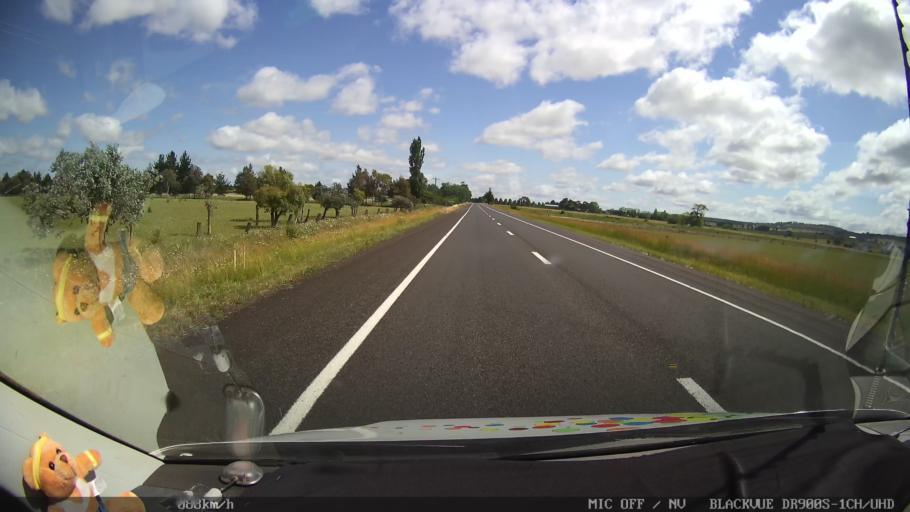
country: AU
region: New South Wales
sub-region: Glen Innes Severn
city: Glen Innes
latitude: -29.8255
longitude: 151.7390
